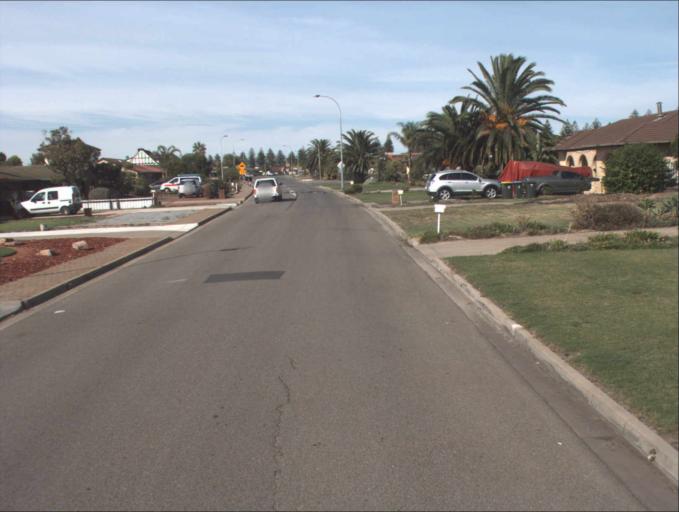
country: AU
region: South Australia
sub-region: Port Adelaide Enfield
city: Birkenhead
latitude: -34.7828
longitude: 138.4930
